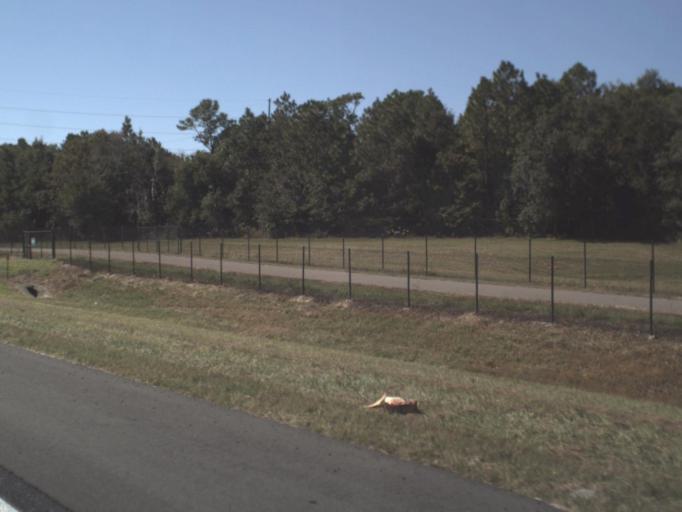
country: US
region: Florida
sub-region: Hernando County
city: Brookridge
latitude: 28.6263
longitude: -82.4918
